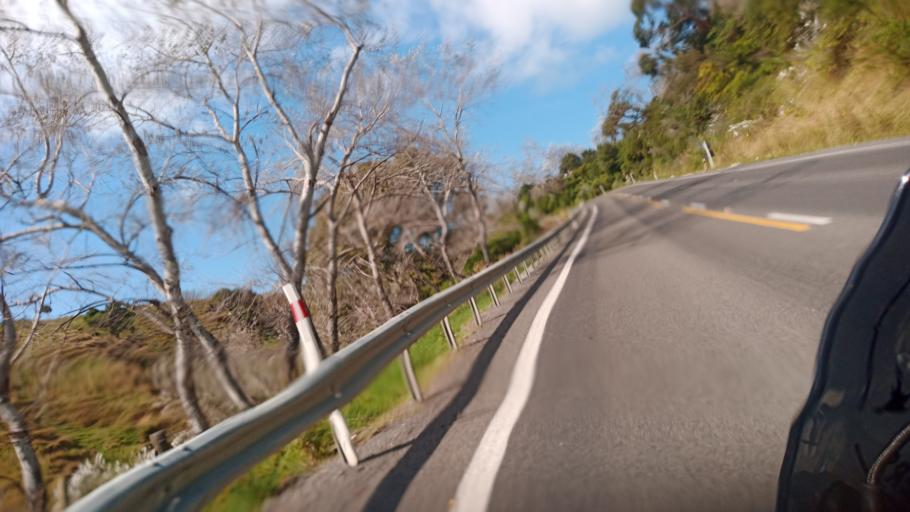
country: NZ
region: Gisborne
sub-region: Gisborne District
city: Gisborne
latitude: -38.4704
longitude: 178.2603
